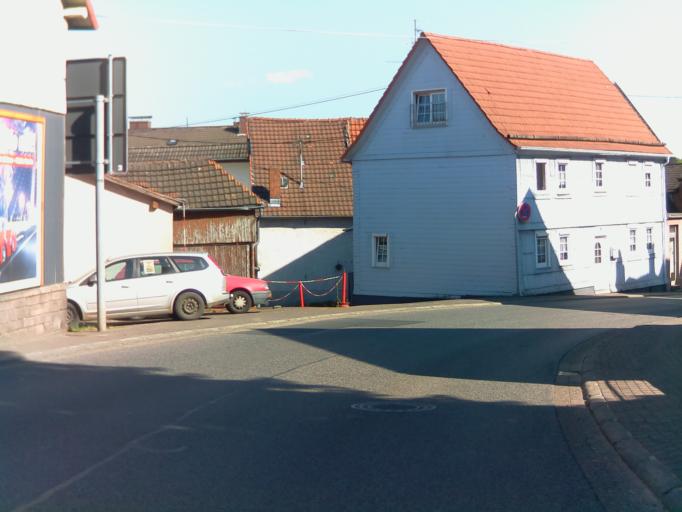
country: DE
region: Hesse
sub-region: Regierungsbezirk Darmstadt
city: Birstein
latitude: 50.3530
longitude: 9.3085
